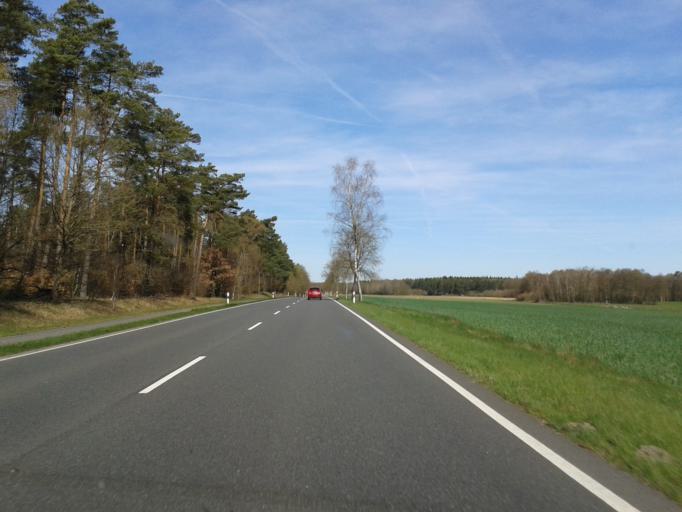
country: DE
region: Lower Saxony
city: Munster
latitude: 52.9638
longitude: 10.1132
